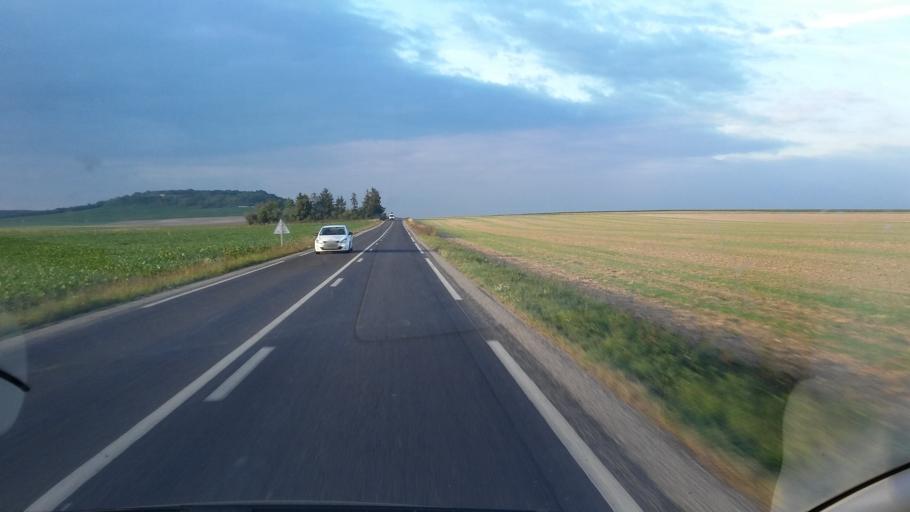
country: FR
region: Champagne-Ardenne
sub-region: Departement de la Marne
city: Vertus
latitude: 48.8403
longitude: 3.9994
